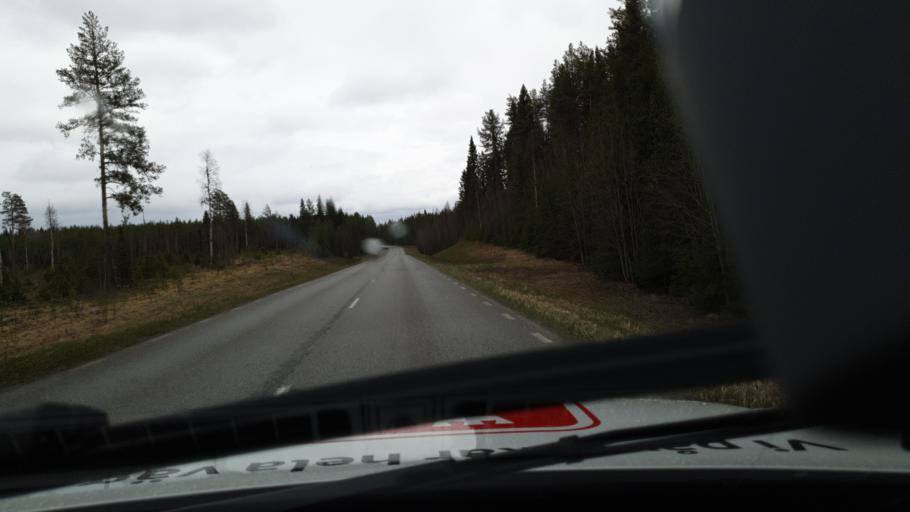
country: SE
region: Jaemtland
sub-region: Stroemsunds Kommun
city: Stroemsund
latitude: 63.6082
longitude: 15.2889
